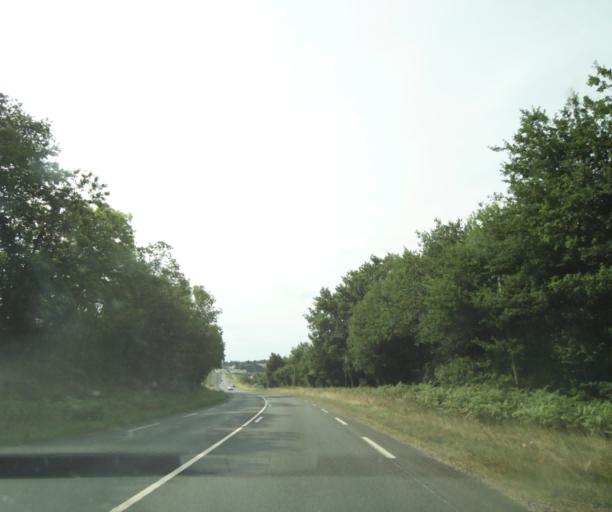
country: FR
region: Pays de la Loire
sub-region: Departement de la Sarthe
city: Ecommoy
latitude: 47.8206
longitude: 0.2971
